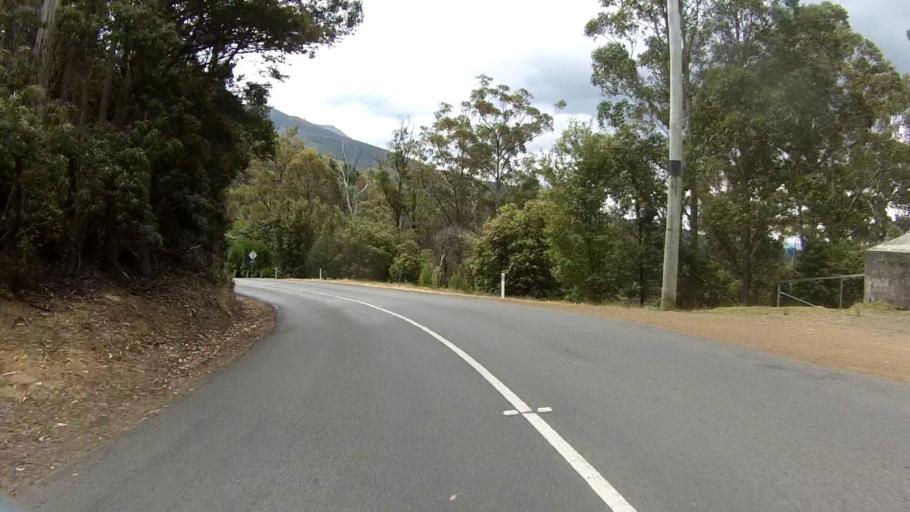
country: AU
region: Tasmania
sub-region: Kingborough
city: Kingston
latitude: -42.9423
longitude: 147.2416
